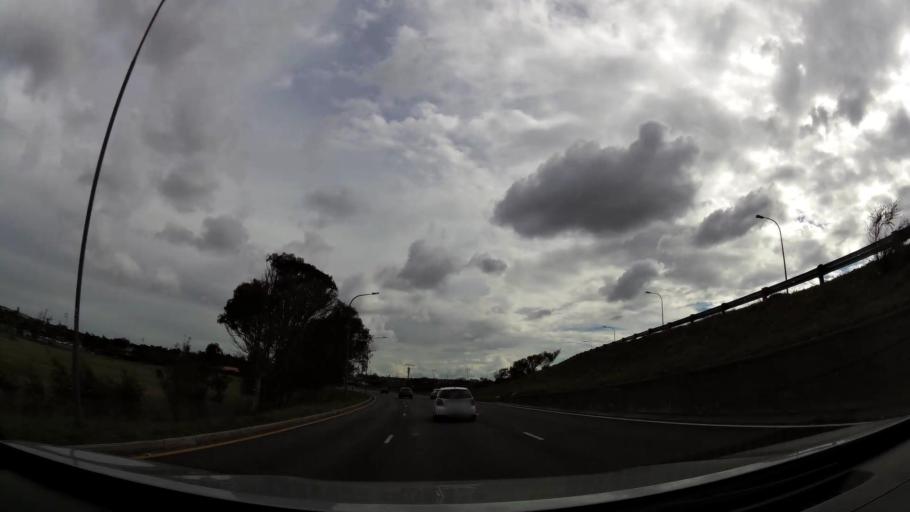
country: ZA
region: Eastern Cape
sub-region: Nelson Mandela Bay Metropolitan Municipality
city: Port Elizabeth
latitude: -33.9454
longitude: 25.5386
